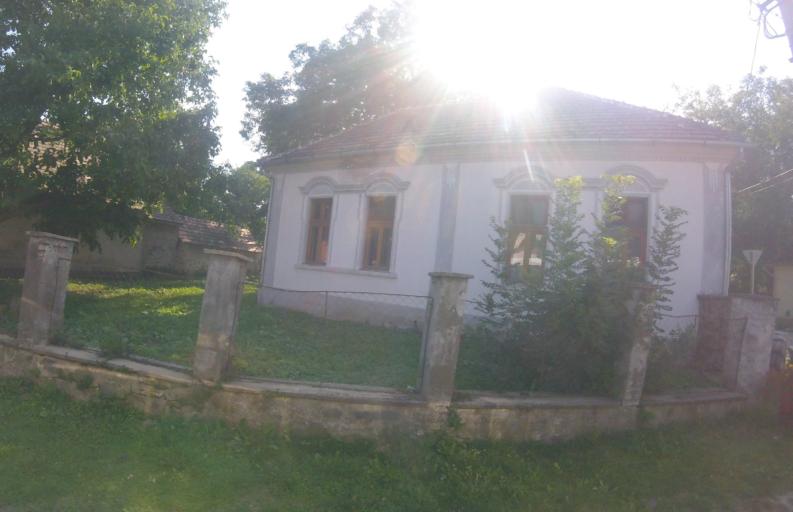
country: HU
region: Zala
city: Cserszegtomaj
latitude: 46.8863
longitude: 17.1939
